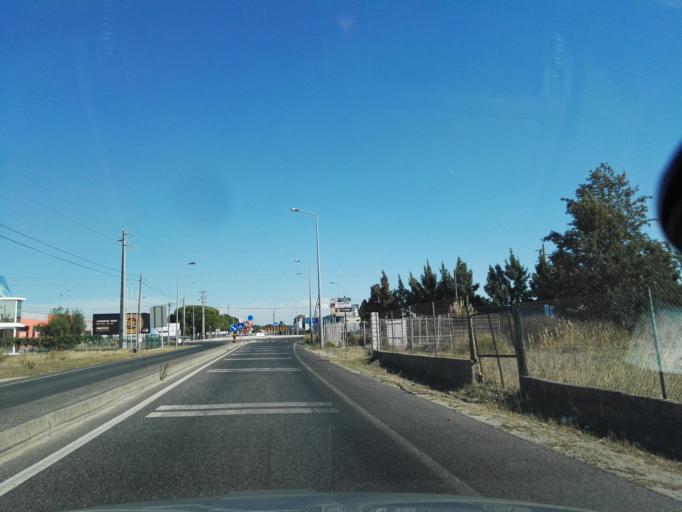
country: PT
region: Santarem
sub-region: Benavente
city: Samora Correia
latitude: 38.9132
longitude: -8.8556
